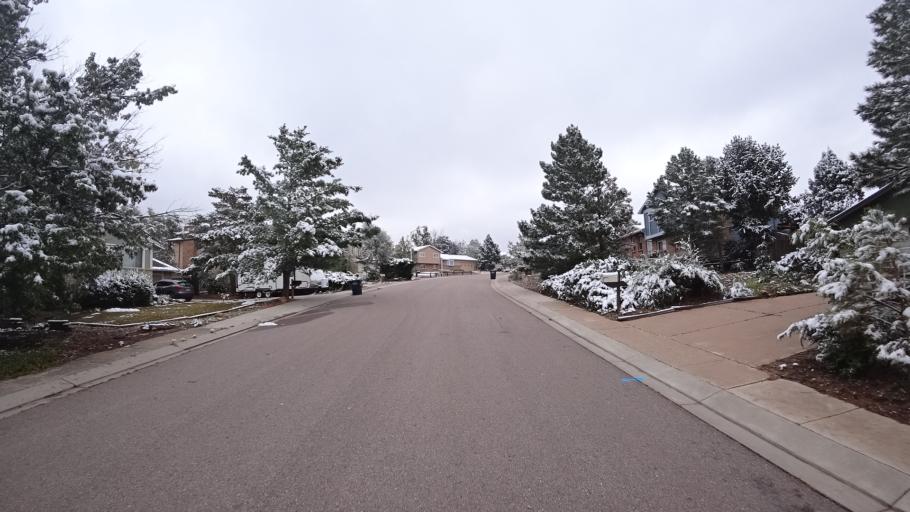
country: US
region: Colorado
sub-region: El Paso County
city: Cimarron Hills
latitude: 38.9209
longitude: -104.7732
